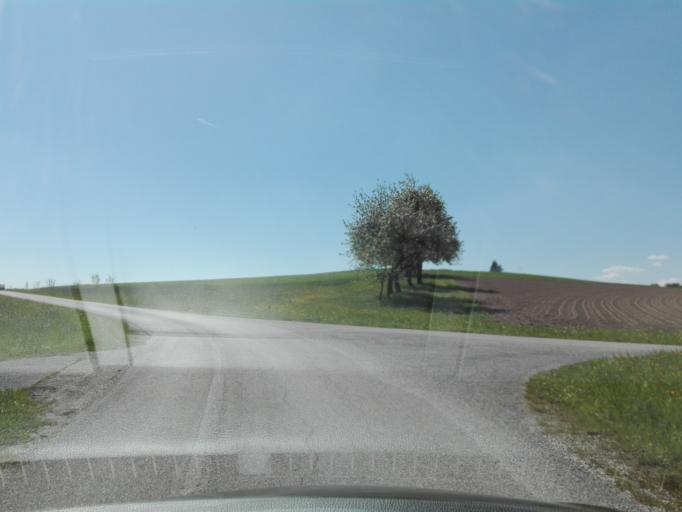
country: AT
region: Upper Austria
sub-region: Politischer Bezirk Urfahr-Umgebung
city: Feldkirchen an der Donau
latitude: 48.3460
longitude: 13.9541
